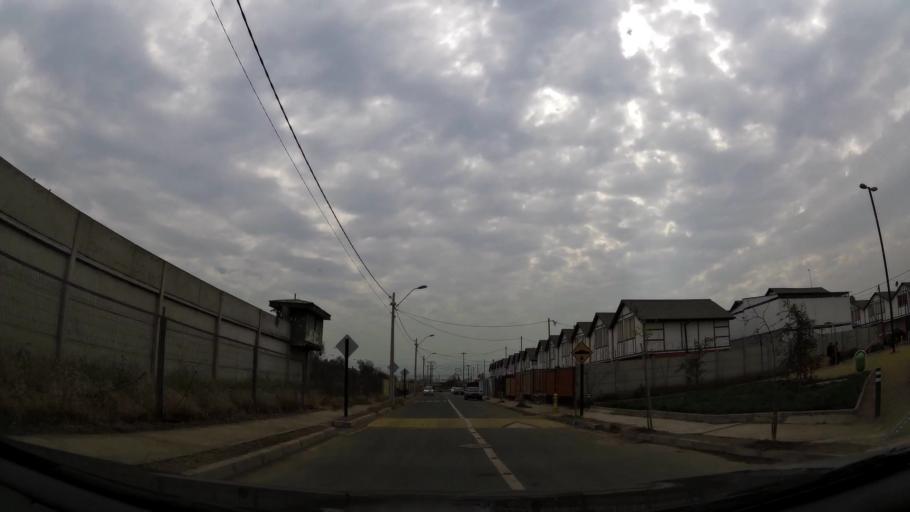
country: CL
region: Santiago Metropolitan
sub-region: Provincia de Chacabuco
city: Chicureo Abajo
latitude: -33.1976
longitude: -70.6683
